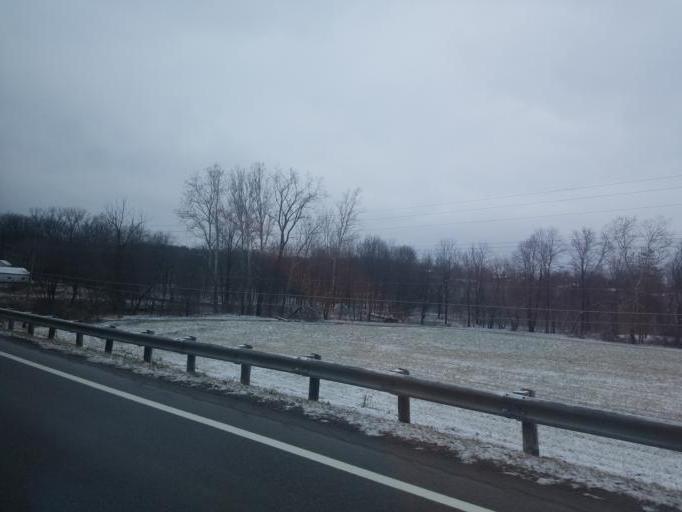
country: US
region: Ohio
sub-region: Licking County
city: Johnstown
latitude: 40.1629
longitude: -82.6938
